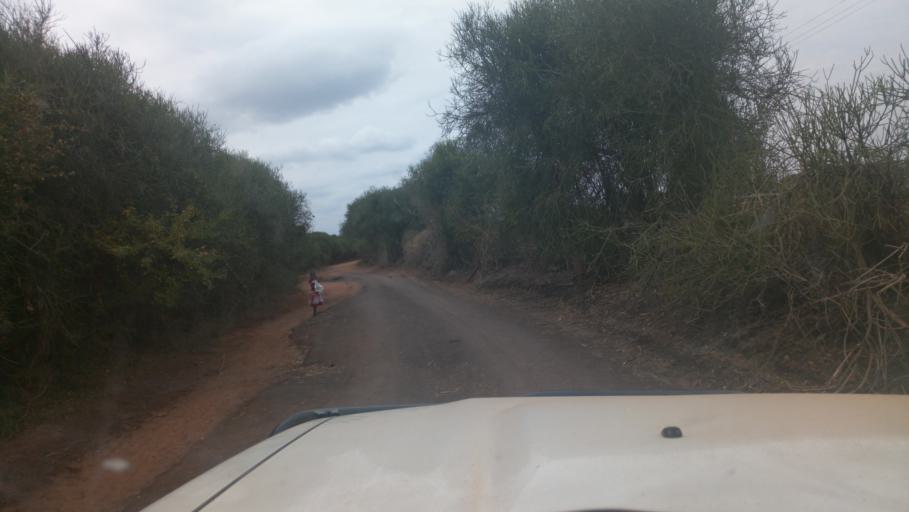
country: KE
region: Makueni
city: Wote
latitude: -1.8434
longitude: 38.0223
